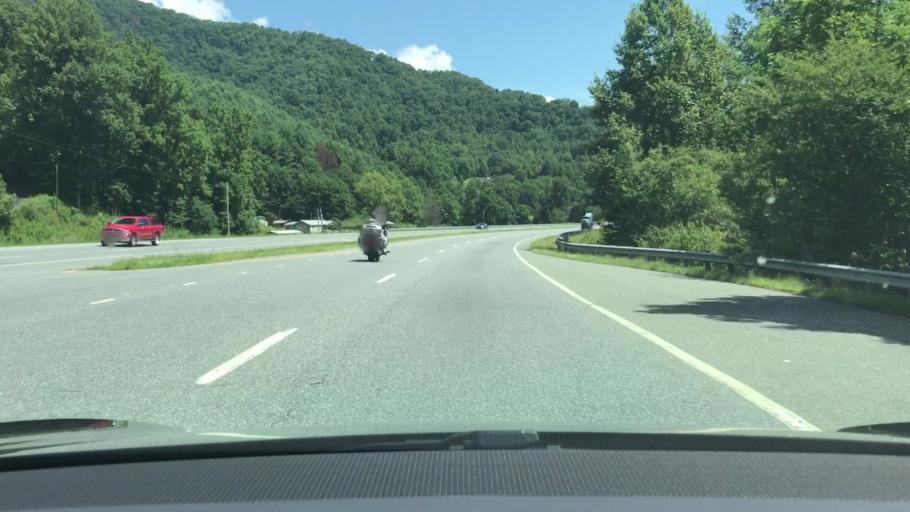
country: US
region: North Carolina
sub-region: Jackson County
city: Sylva
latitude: 35.2888
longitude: -83.2831
